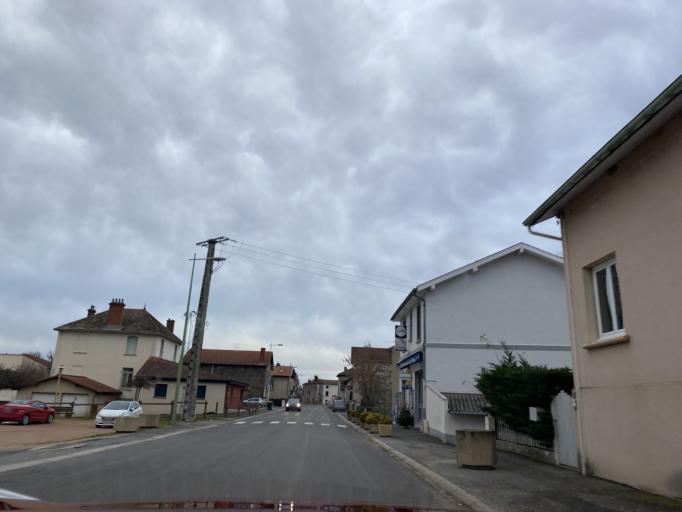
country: FR
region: Auvergne
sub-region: Departement du Puy-de-Dome
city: Peschadoires
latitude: 45.8369
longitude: 3.4994
